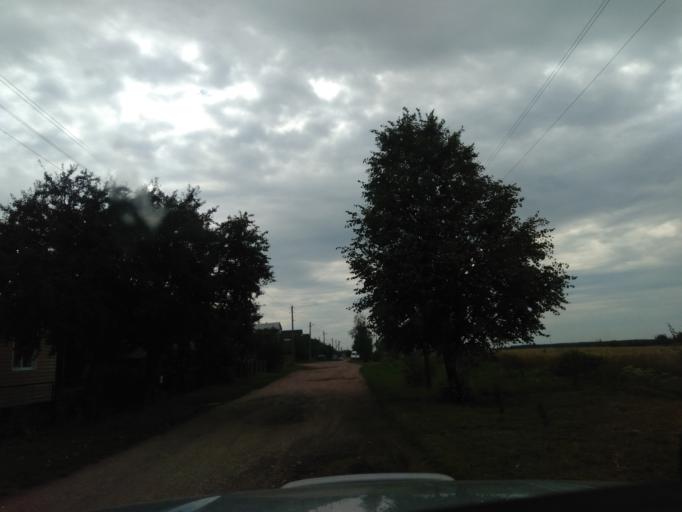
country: BY
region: Minsk
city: Kapyl'
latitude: 53.1518
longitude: 27.0715
